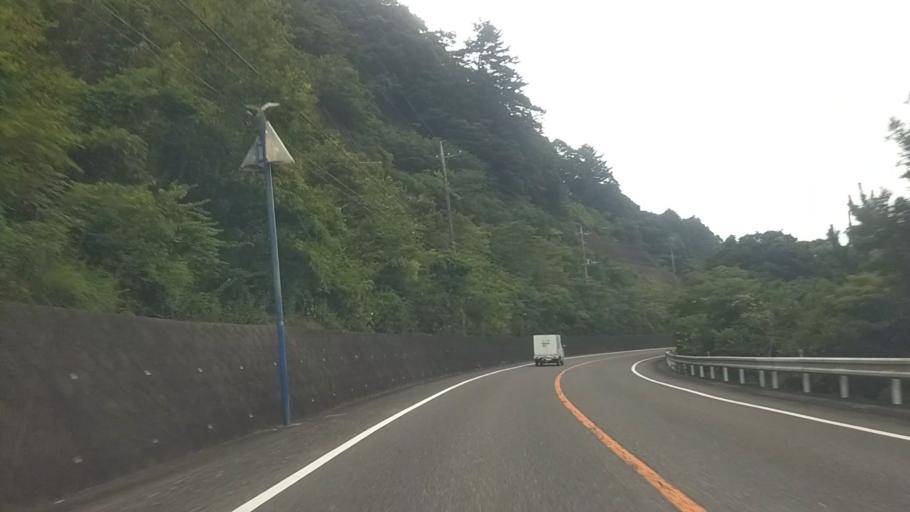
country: JP
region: Chiba
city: Kawaguchi
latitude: 35.1535
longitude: 140.0675
